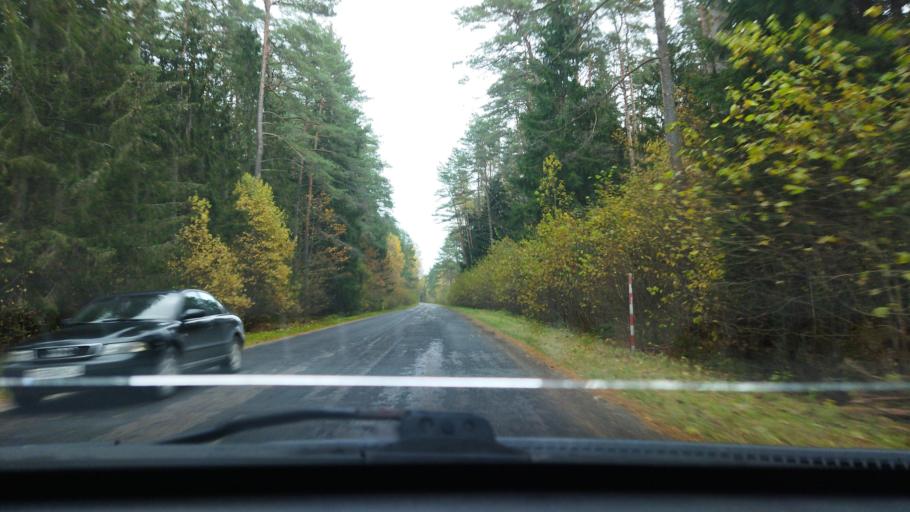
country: BY
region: Minsk
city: Svir
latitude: 54.8136
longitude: 26.1958
